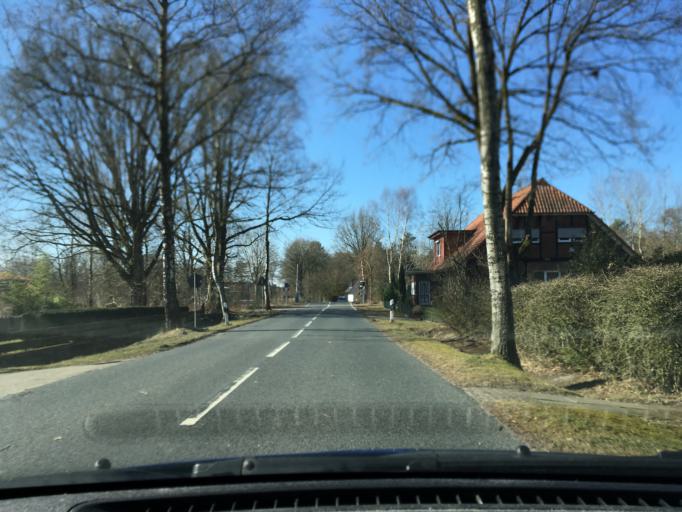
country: DE
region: Lower Saxony
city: Schneverdingen
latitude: 53.0794
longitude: 9.8125
